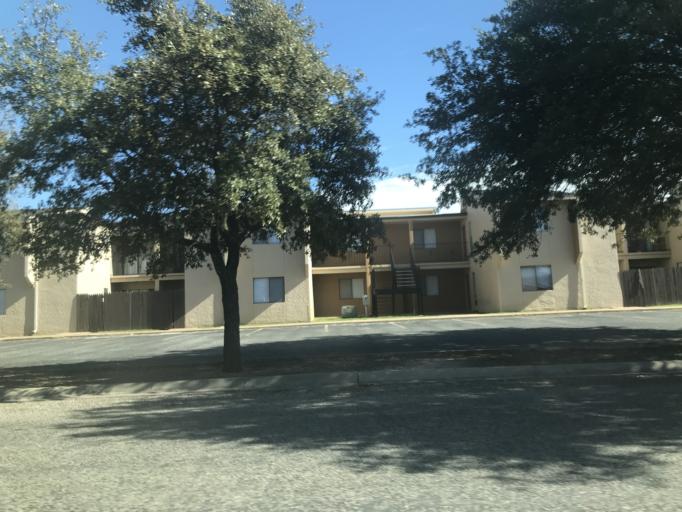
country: US
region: Texas
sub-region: Tom Green County
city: San Angelo
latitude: 31.4237
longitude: -100.4879
